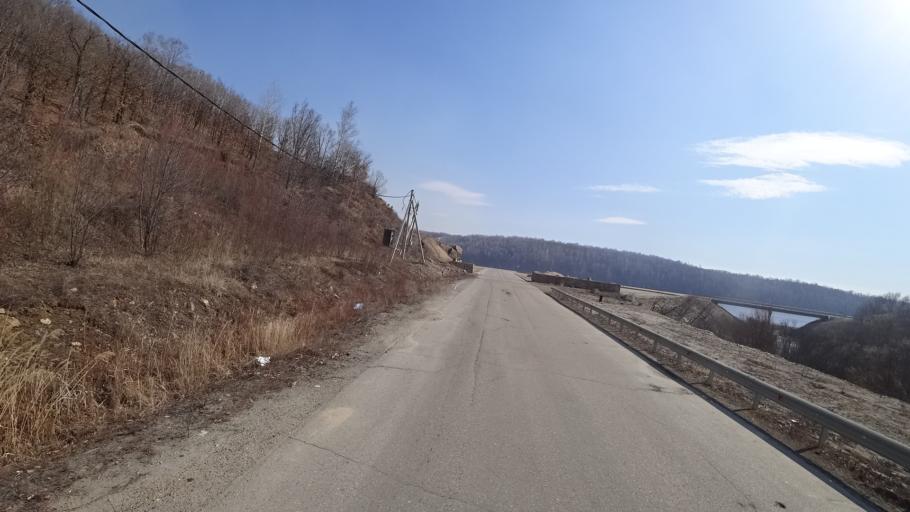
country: RU
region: Amur
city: Novobureyskiy
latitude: 49.7911
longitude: 129.9648
